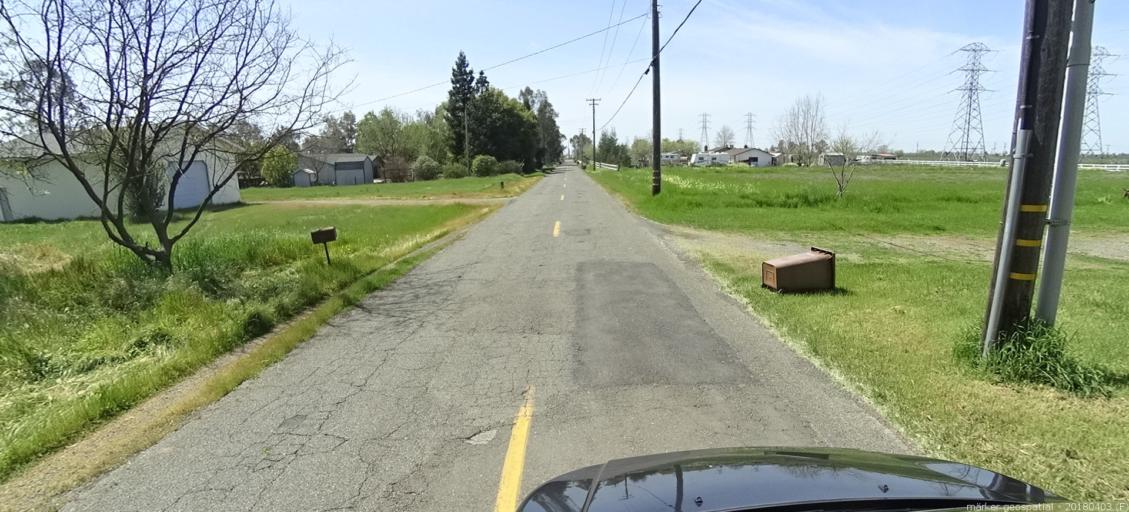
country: US
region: California
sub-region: Sacramento County
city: Herald
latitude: 38.3506
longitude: -121.2368
